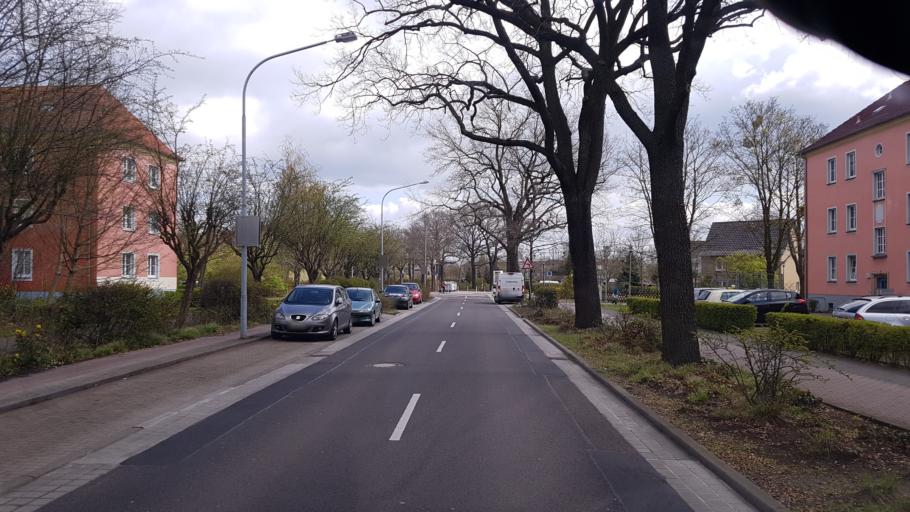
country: DE
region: Brandenburg
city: Senftenberg
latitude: 51.5211
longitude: 13.9855
